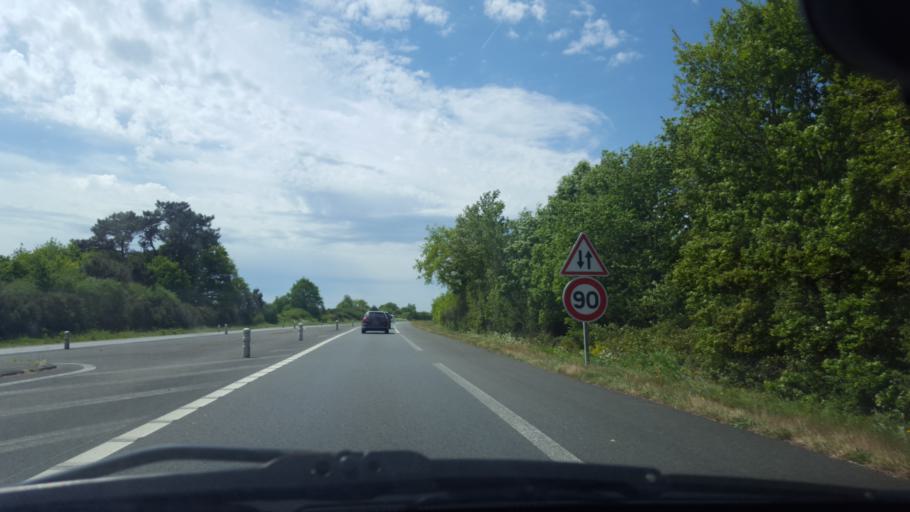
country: FR
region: Pays de la Loire
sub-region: Departement de la Loire-Atlantique
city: Paulx
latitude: 47.0024
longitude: -1.7260
